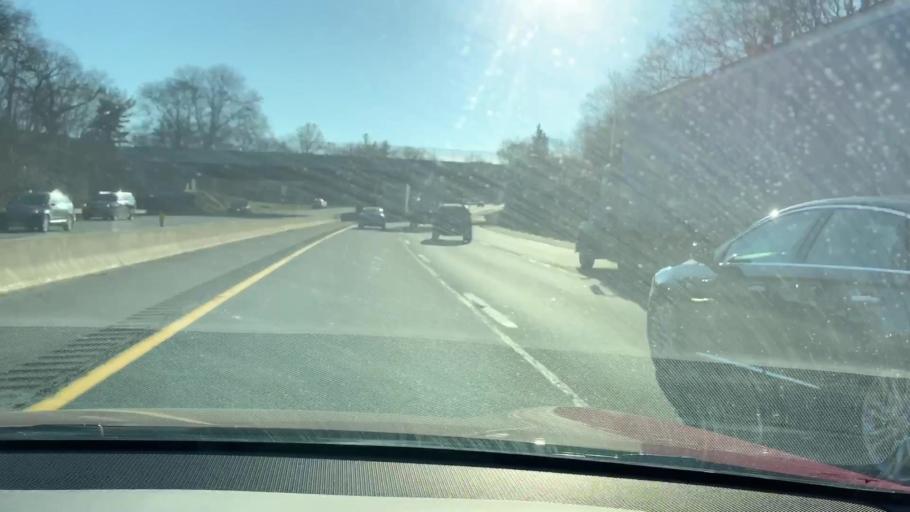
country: US
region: New York
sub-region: Westchester County
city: Port Chester
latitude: 40.9995
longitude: -73.6824
